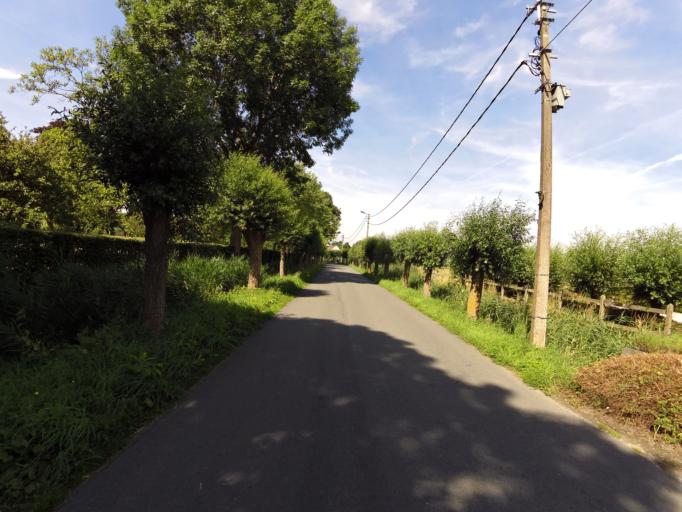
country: BE
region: Flanders
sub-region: Provincie West-Vlaanderen
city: Damme
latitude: 51.2776
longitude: 3.3006
